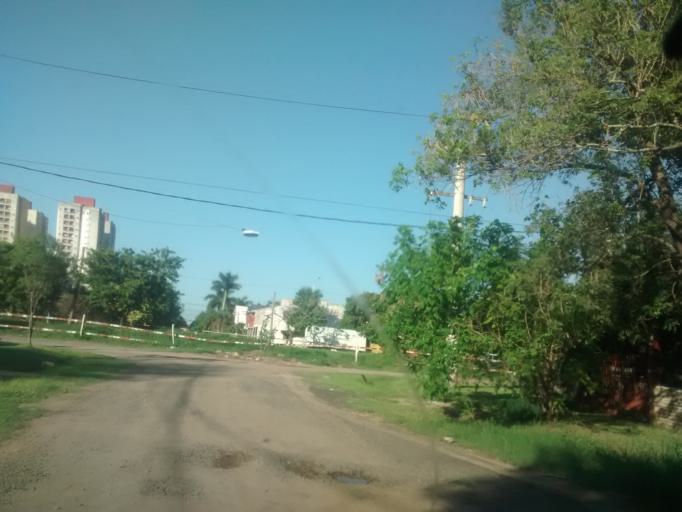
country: AR
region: Chaco
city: Resistencia
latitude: -27.4442
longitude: -59.0039
